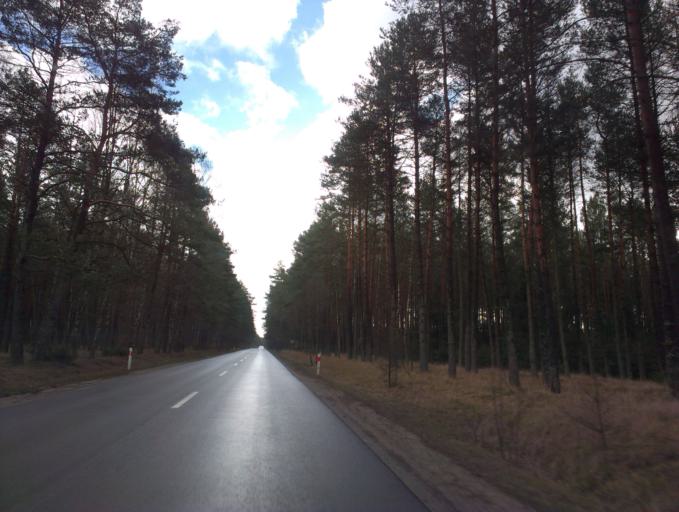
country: PL
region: Pomeranian Voivodeship
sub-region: Powiat czluchowski
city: Czarne
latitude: 53.6989
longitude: 16.8872
